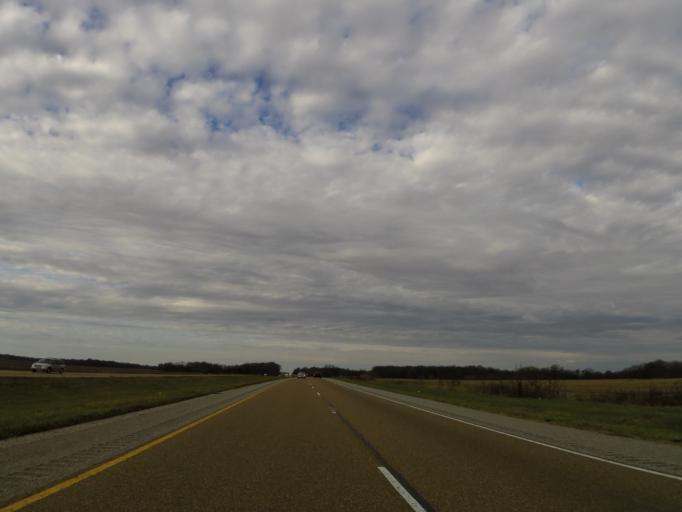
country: US
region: Illinois
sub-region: Clinton County
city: Wamac
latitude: 38.3889
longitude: -89.1957
